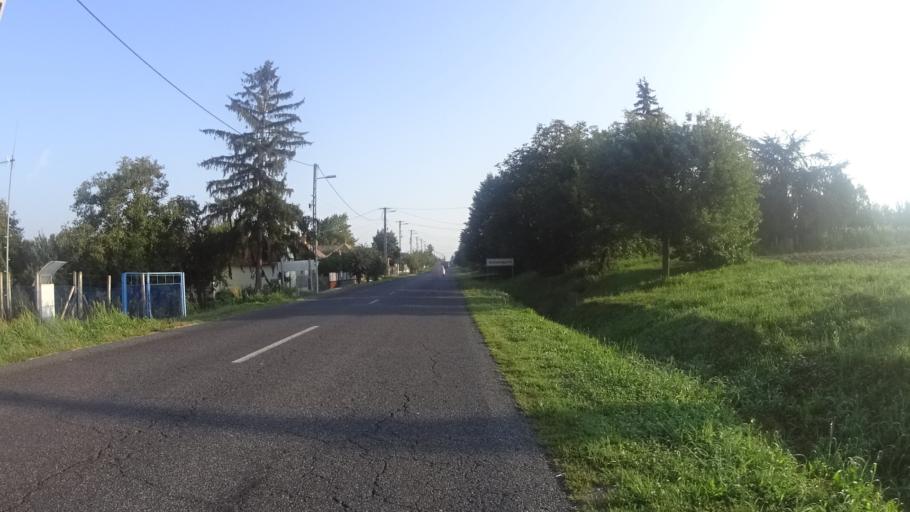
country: HU
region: Zala
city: Zalakomar
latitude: 46.5861
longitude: 17.1768
